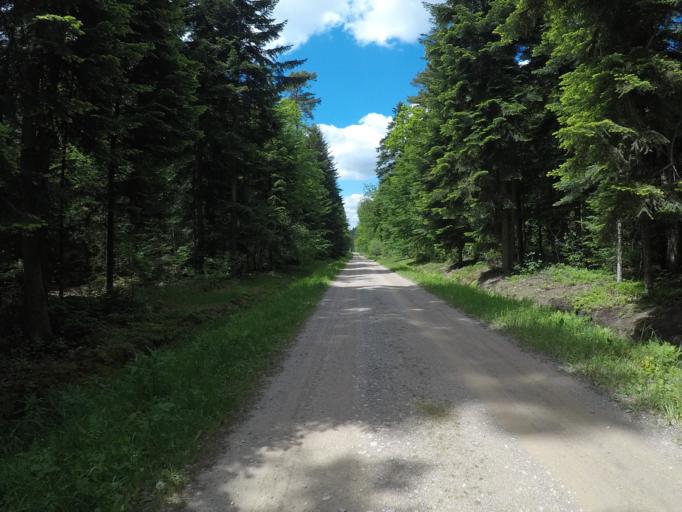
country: PL
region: Swietokrzyskie
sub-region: Powiat kielecki
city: Kostomloty Pierwsze
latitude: 50.9303
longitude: 20.6394
